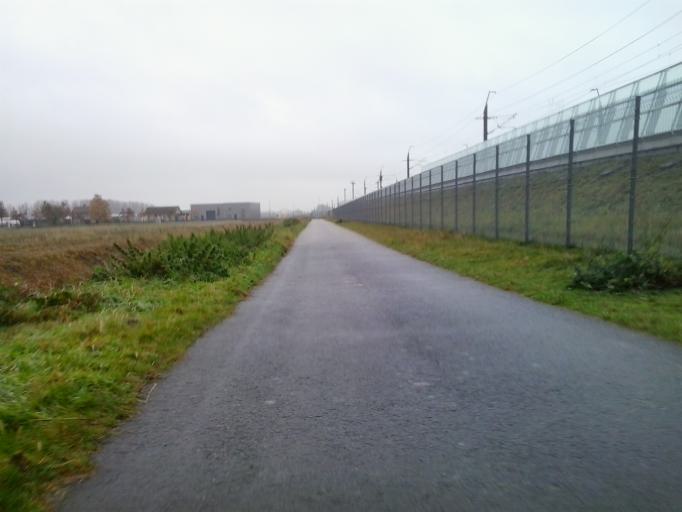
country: NL
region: South Holland
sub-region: Gemeente Lansingerland
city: Berkel en Rodenrijs
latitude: 51.9809
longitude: 4.4734
